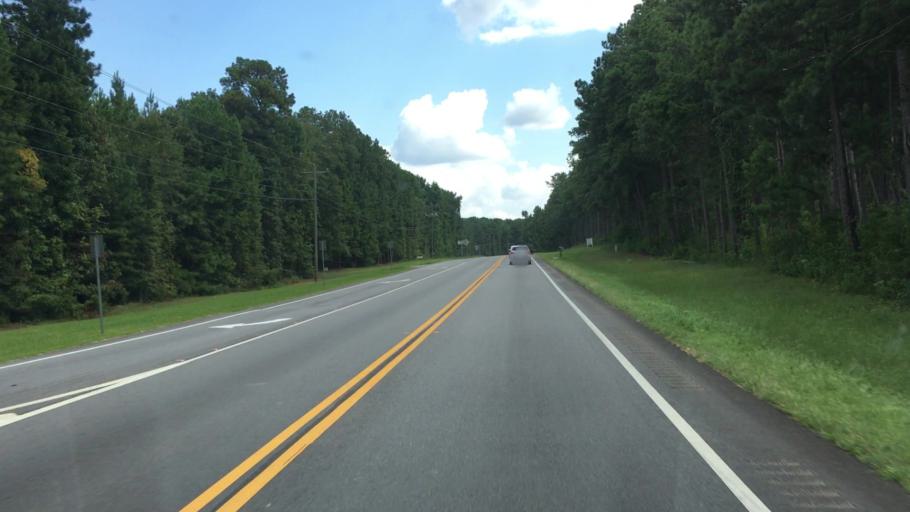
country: US
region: Georgia
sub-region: Putnam County
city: Jefferson
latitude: 33.4106
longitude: -83.3706
